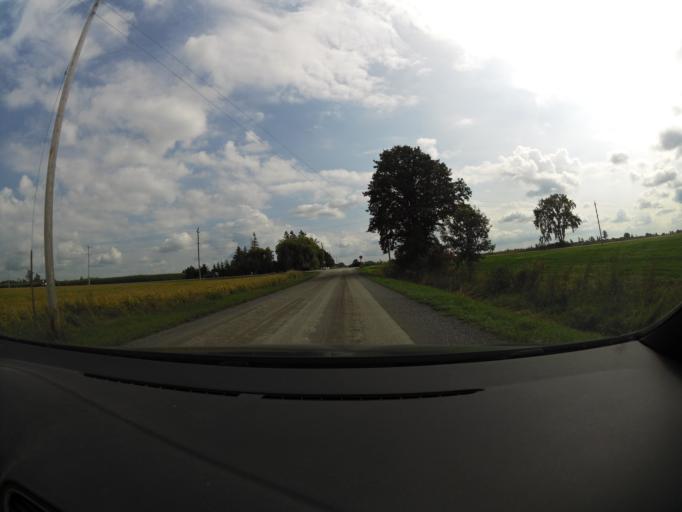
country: CA
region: Ontario
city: Arnprior
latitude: 45.3761
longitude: -76.2163
